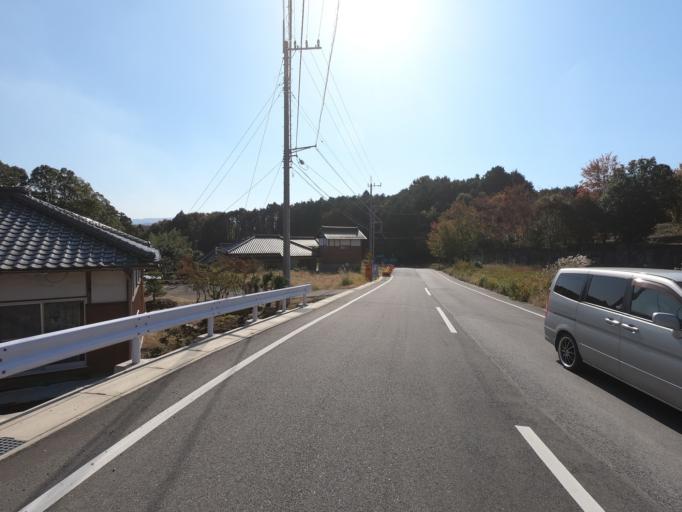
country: JP
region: Ibaraki
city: Tsukuba
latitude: 36.2296
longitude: 140.1411
